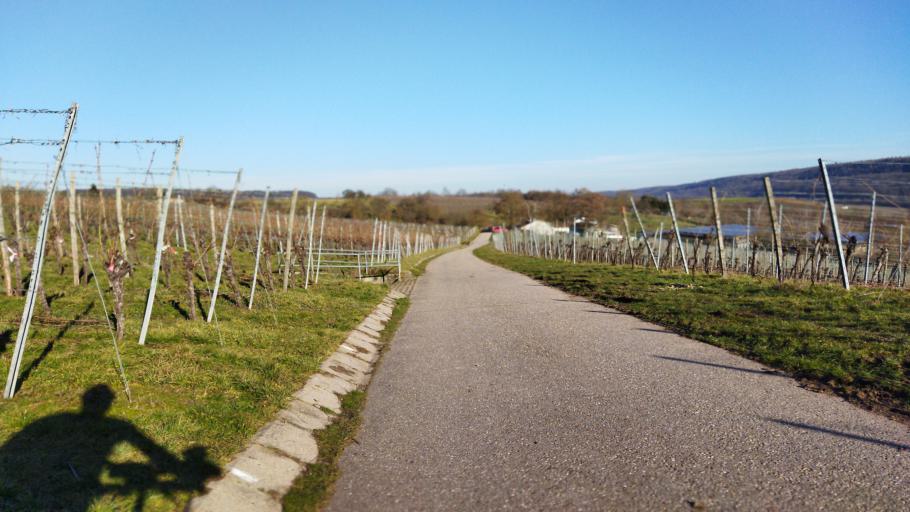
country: DE
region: Baden-Wuerttemberg
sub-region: Regierungsbezirk Stuttgart
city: Erlenbach
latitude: 49.1751
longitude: 9.2877
